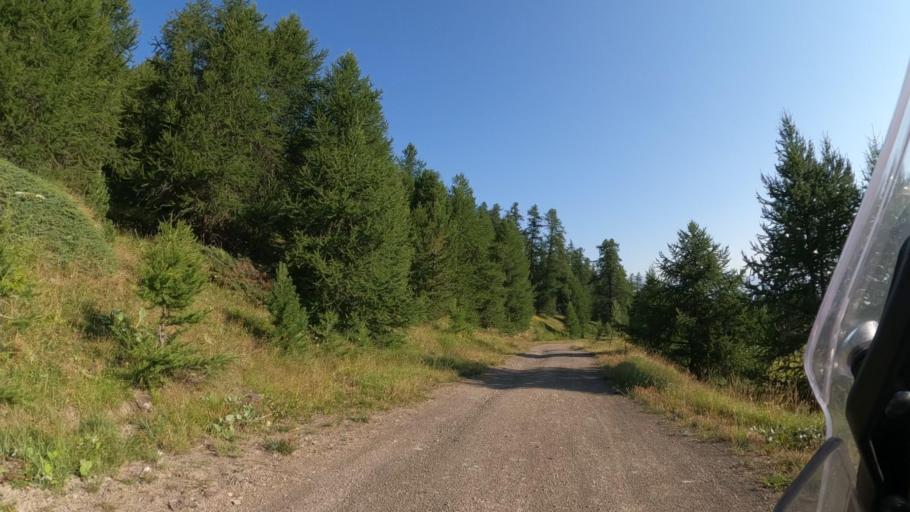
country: FR
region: Provence-Alpes-Cote d'Azur
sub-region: Departement des Hautes-Alpes
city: Guillestre
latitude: 44.6139
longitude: 6.6459
